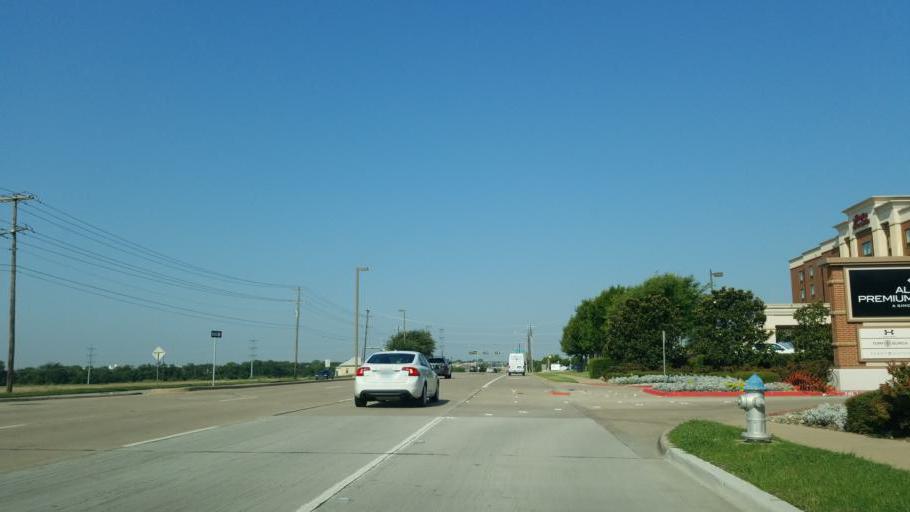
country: US
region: Texas
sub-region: Collin County
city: Allen
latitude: 33.1300
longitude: -96.6615
